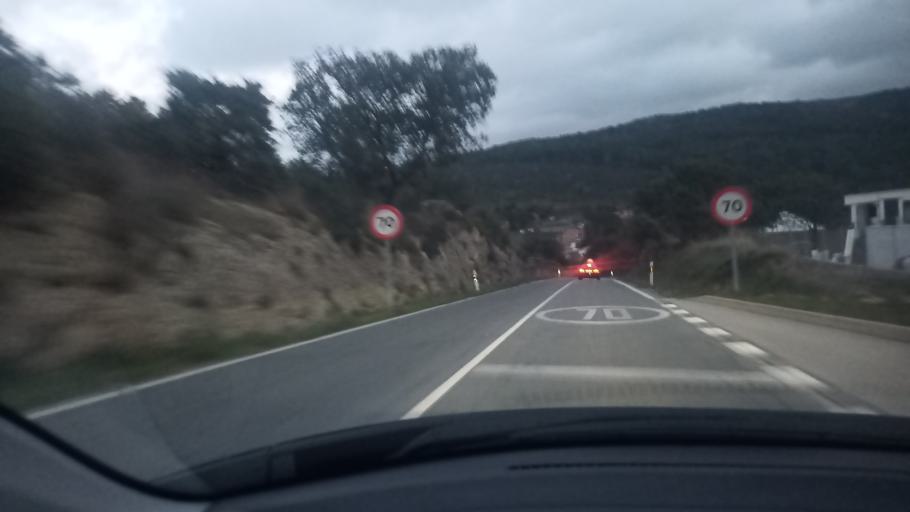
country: ES
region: Madrid
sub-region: Provincia de Madrid
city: Robledo de Chavela
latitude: 40.5099
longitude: -4.2369
